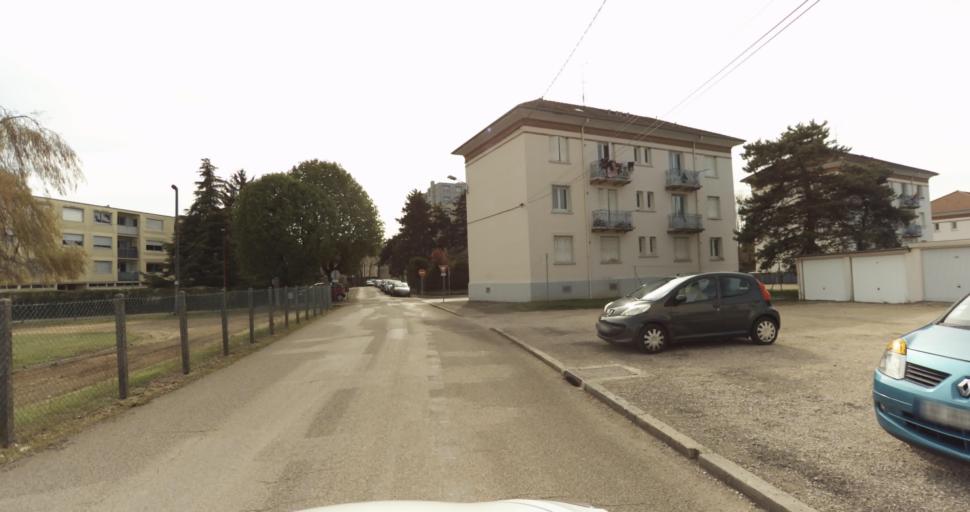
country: FR
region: Rhone-Alpes
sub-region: Departement de l'Ain
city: Amberieu-en-Bugey
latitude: 45.9550
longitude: 5.3484
